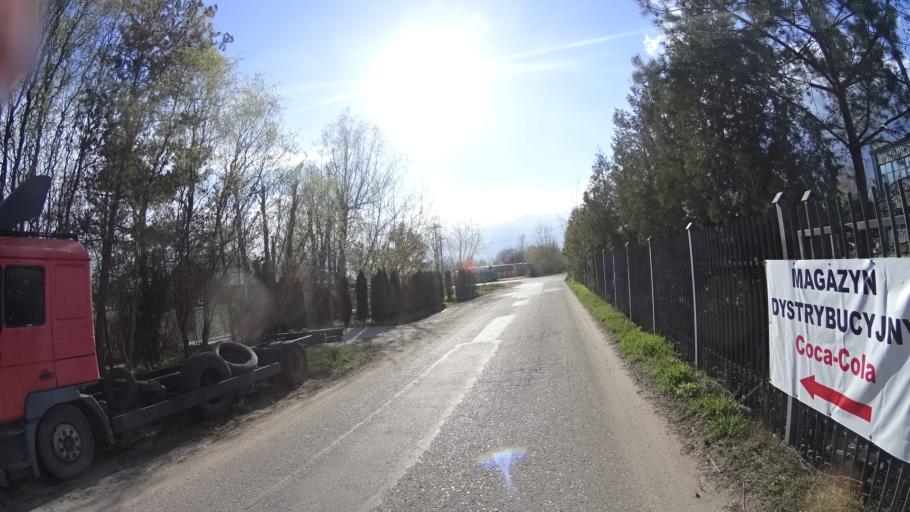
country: PL
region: Masovian Voivodeship
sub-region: Powiat warszawski zachodni
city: Babice
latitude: 52.2820
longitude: 20.8681
